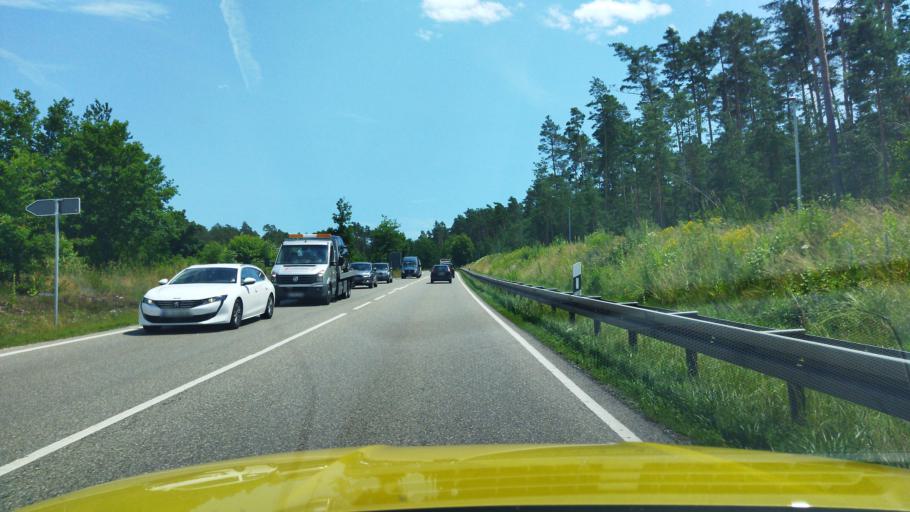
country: DE
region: Bavaria
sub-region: Regierungsbezirk Mittelfranken
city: Roth
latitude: 49.2446
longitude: 11.1195
